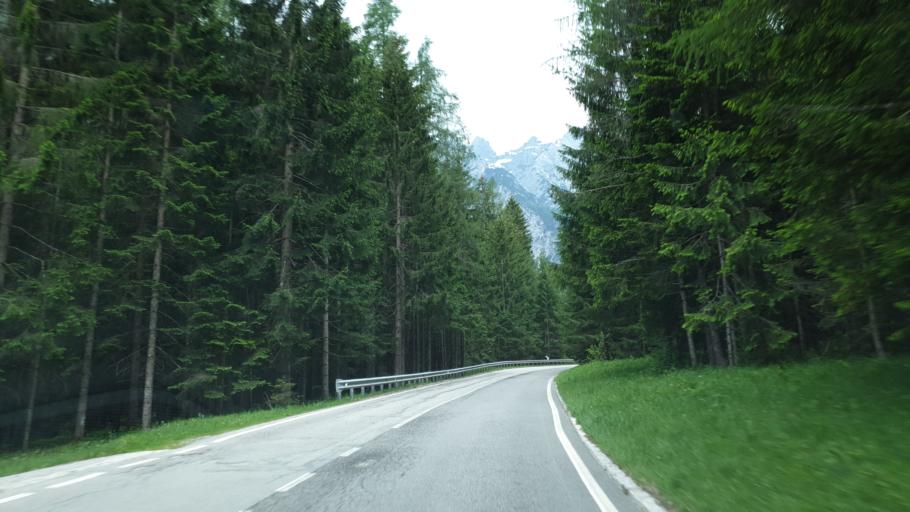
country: IT
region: Veneto
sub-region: Provincia di Belluno
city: Auronzo
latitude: 46.5449
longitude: 12.3242
